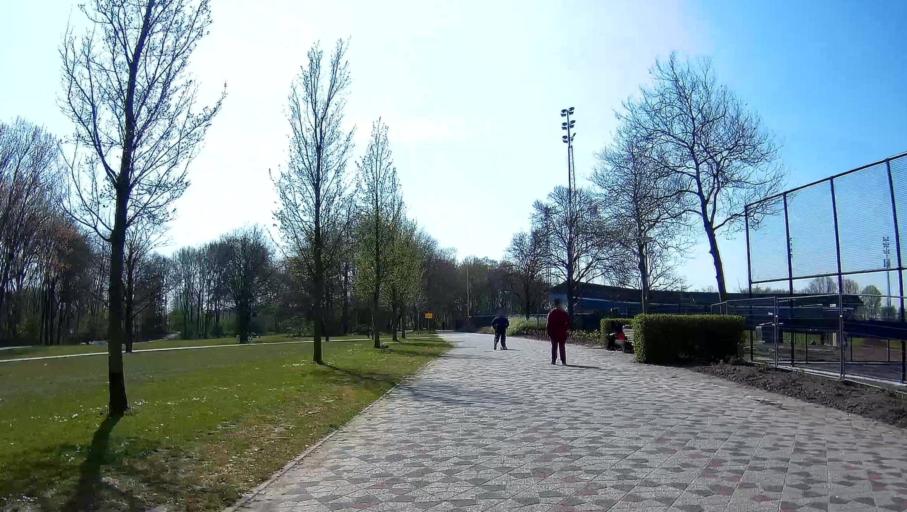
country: NL
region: South Holland
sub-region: Gemeente Rotterdam
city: Delfshaven
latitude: 51.9252
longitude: 4.4410
